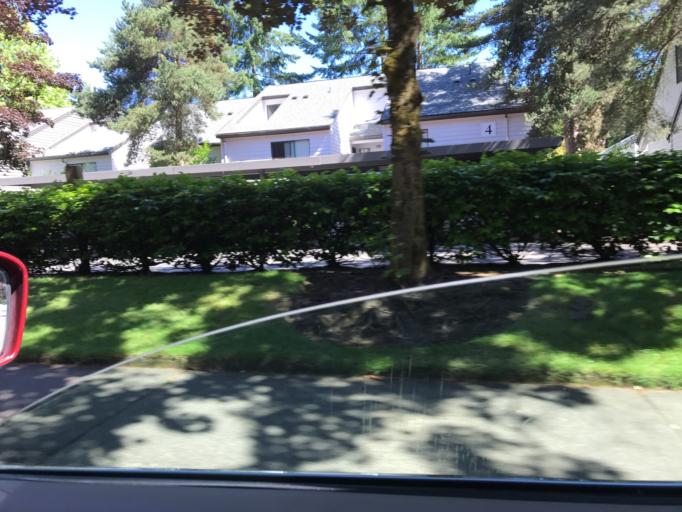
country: US
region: Washington
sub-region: King County
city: Redmond
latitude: 47.6459
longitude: -122.1446
